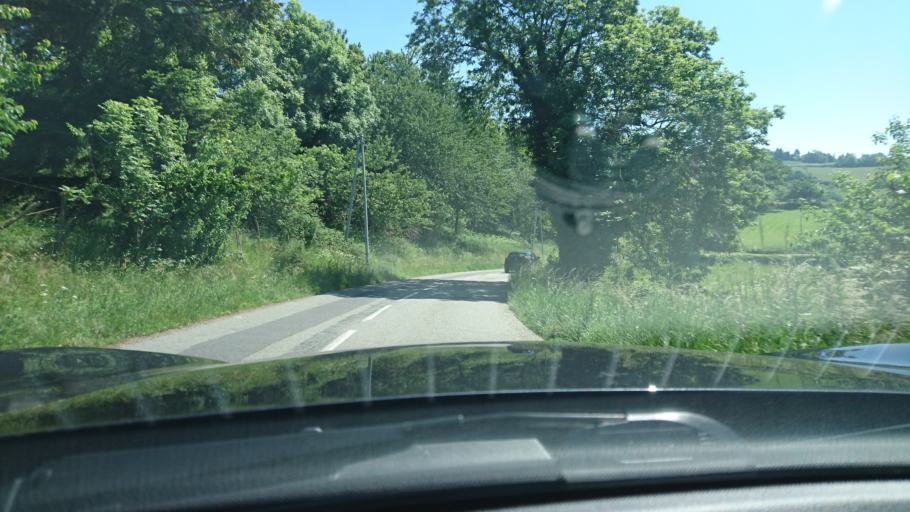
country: FR
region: Rhone-Alpes
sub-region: Departement de la Loire
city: Bussieres
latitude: 45.8433
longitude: 4.2666
